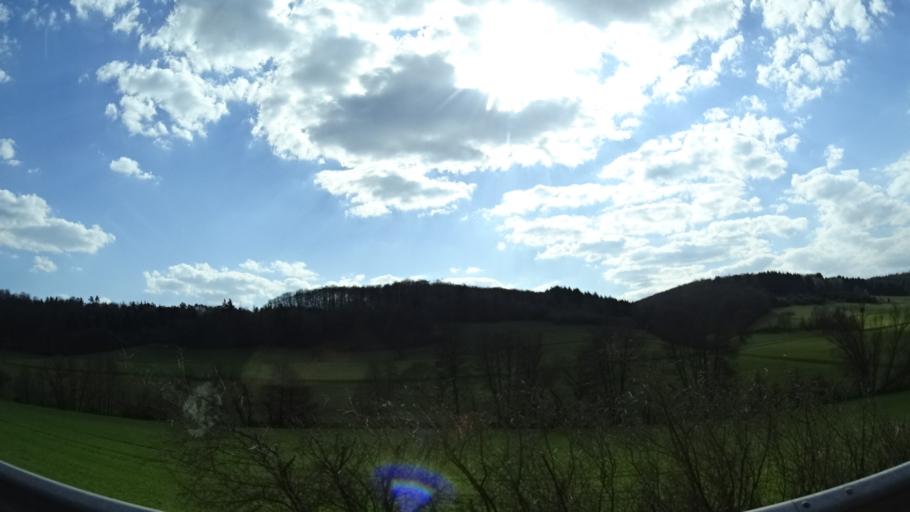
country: DE
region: Rheinland-Pfalz
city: Mittelreidenbach
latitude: 49.7387
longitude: 7.4563
